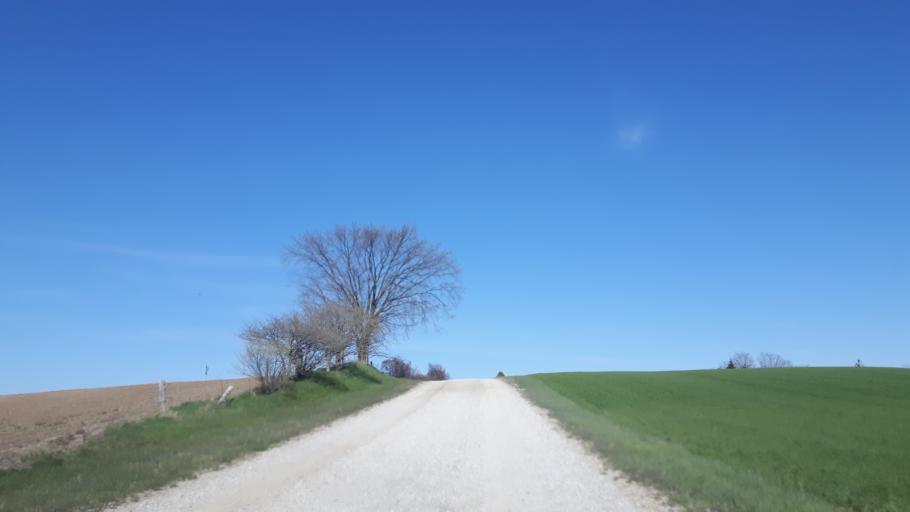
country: CA
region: Ontario
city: Goderich
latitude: 43.6613
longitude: -81.6812
